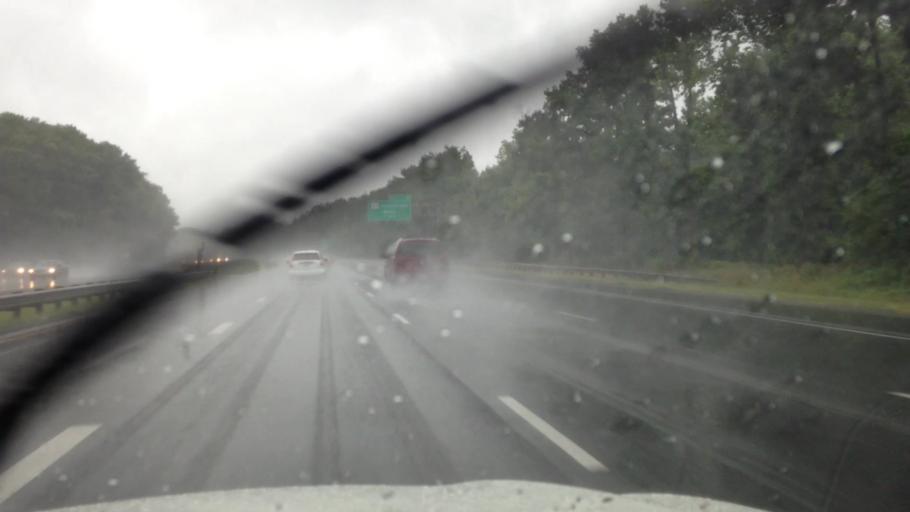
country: US
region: Maryland
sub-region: Prince George's County
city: Mitchellville
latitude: 38.9455
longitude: -76.7664
